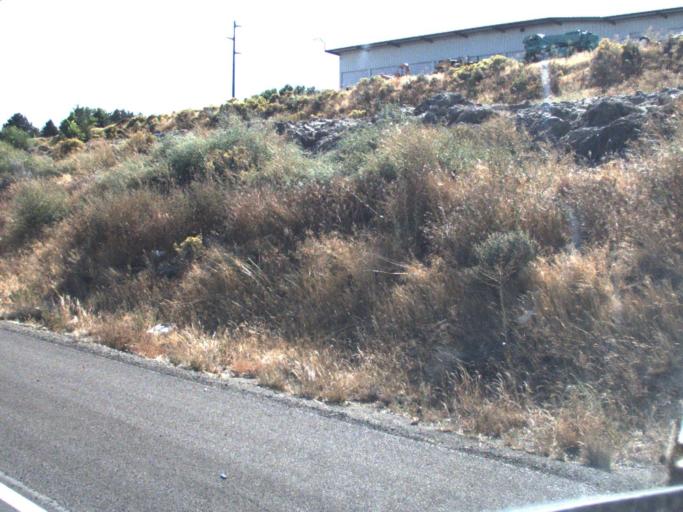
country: US
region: Washington
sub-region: Franklin County
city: West Pasco
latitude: 46.2261
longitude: -119.1787
